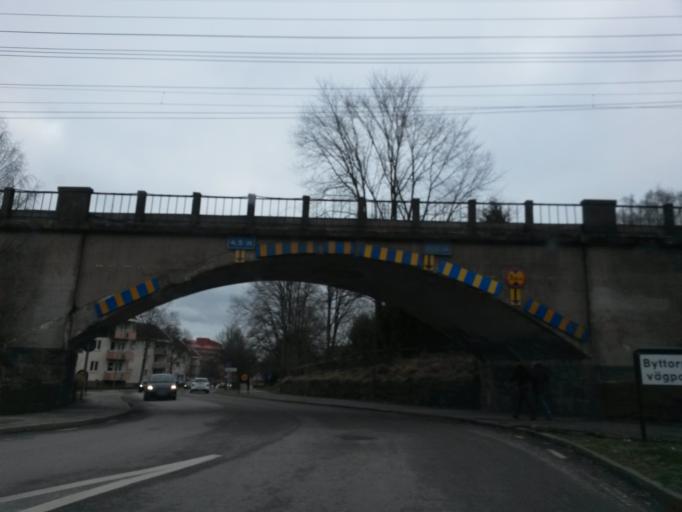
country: SE
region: Vaestra Goetaland
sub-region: Boras Kommun
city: Boras
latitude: 57.7256
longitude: 12.9229
